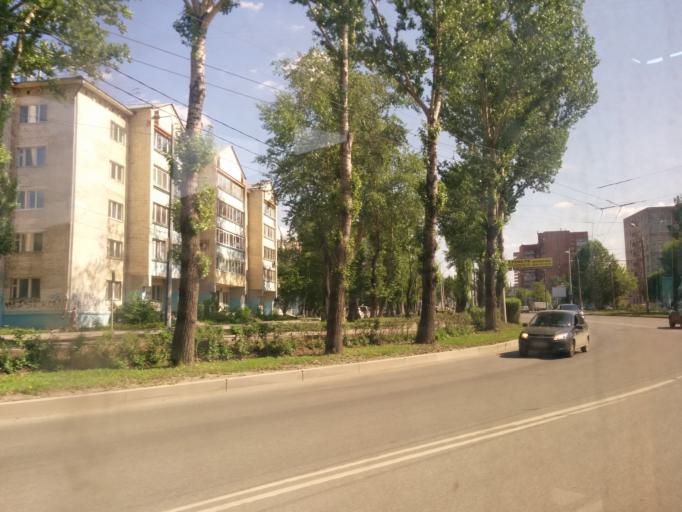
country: RU
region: Perm
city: Perm
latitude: 58.0120
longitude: 56.2799
